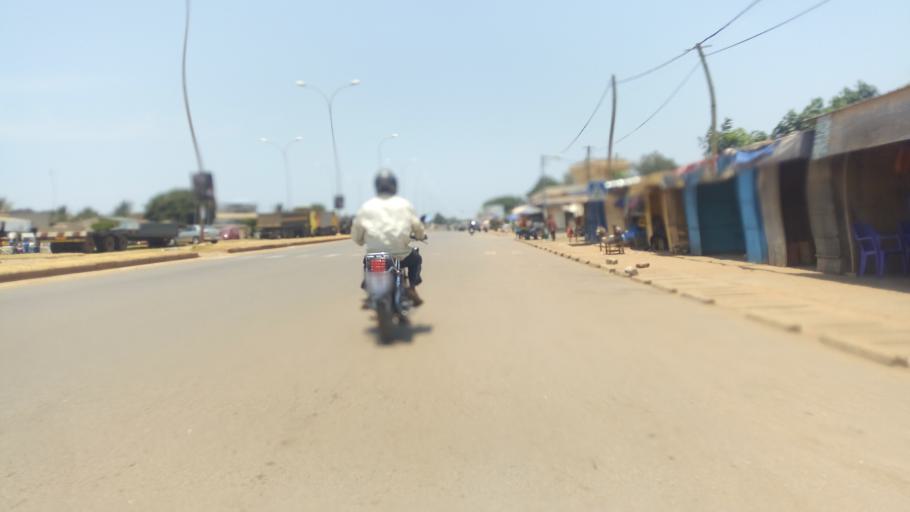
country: TG
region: Maritime
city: Lome
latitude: 6.2284
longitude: 1.1945
